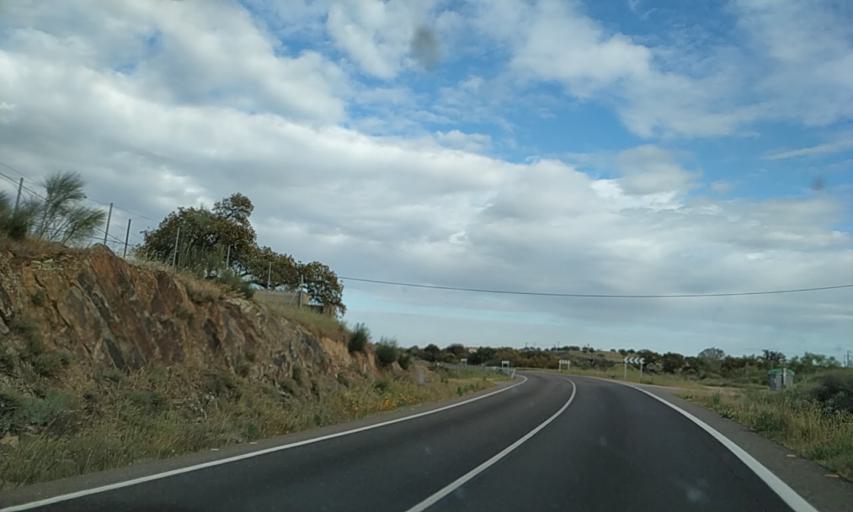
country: ES
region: Extremadura
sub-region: Provincia de Caceres
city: Huelaga
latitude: 40.0359
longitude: -6.6264
